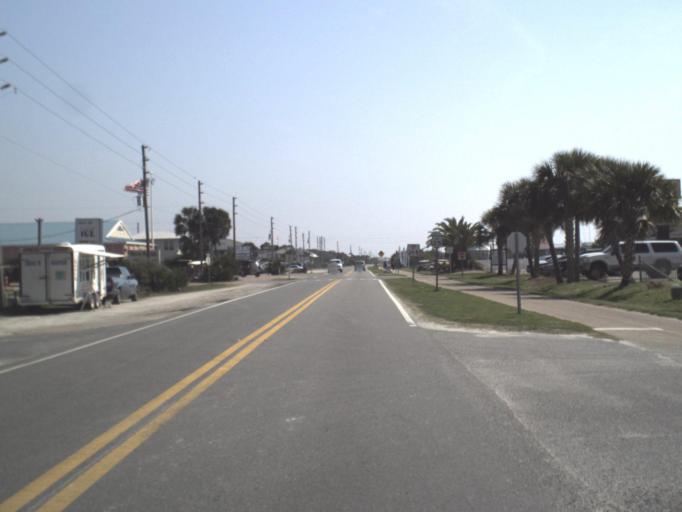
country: US
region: Florida
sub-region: Franklin County
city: Eastpoint
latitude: 29.6636
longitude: -84.8623
